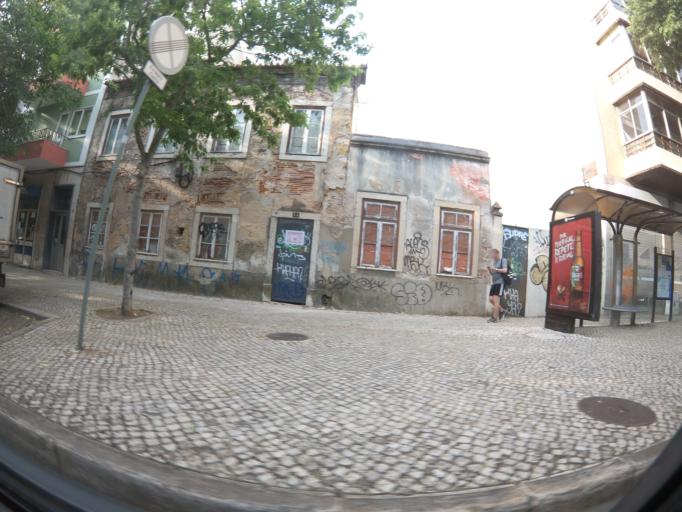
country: PT
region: Lisbon
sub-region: Oeiras
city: Alges
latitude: 38.6960
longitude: -9.2189
